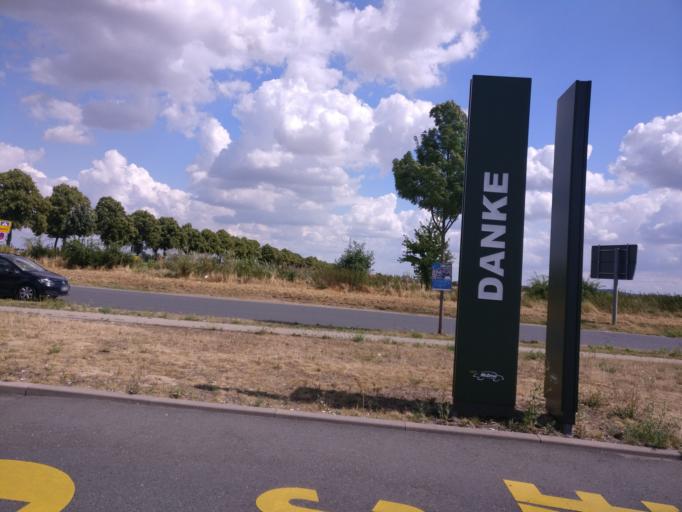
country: DE
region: Lower Saxony
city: Hildesheim
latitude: 52.1607
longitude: 9.9979
